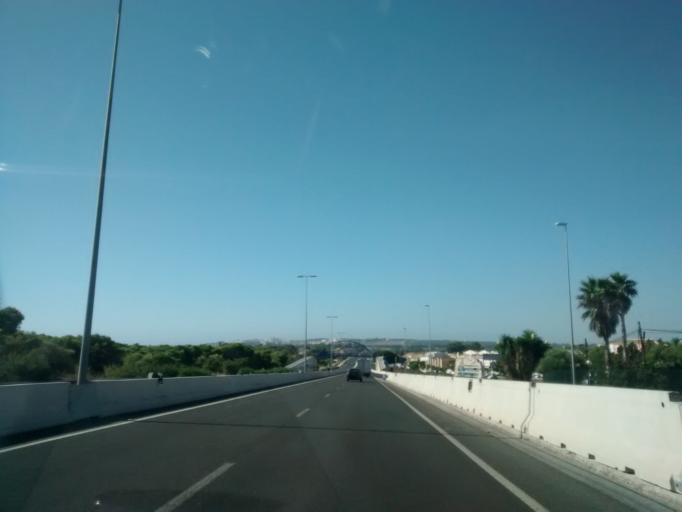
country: ES
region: Valencia
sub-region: Provincia de Alicante
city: Guardamar del Segura
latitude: 38.0583
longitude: -0.6568
